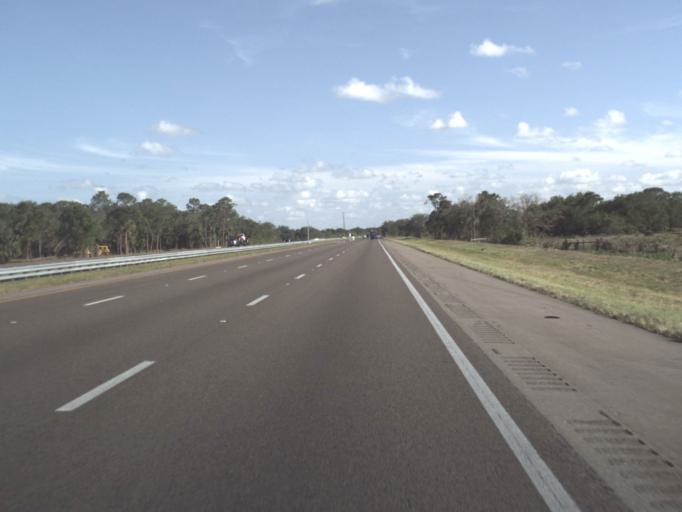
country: US
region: Florida
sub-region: Brevard County
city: Grant-Valkaria
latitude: 27.8938
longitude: -80.5945
